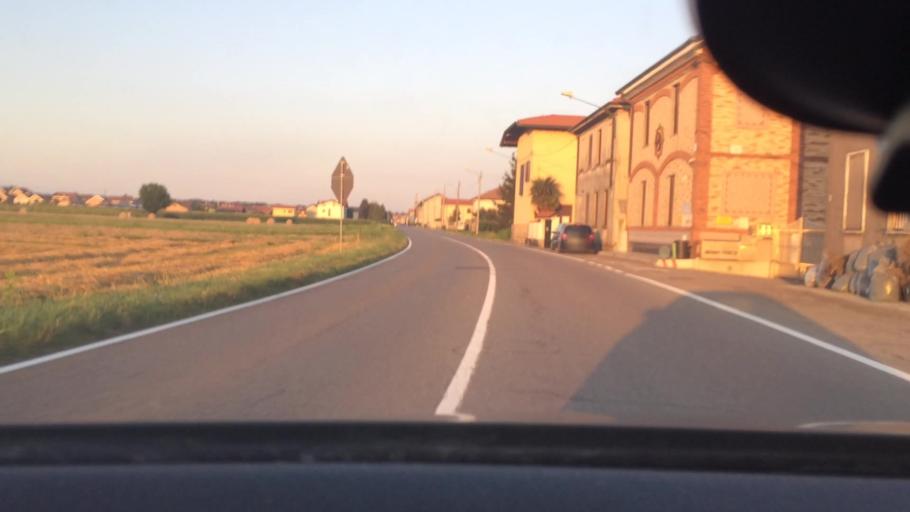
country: IT
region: Lombardy
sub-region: Provincia di Monza e Brianza
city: Cogliate
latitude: 45.6463
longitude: 9.0652
